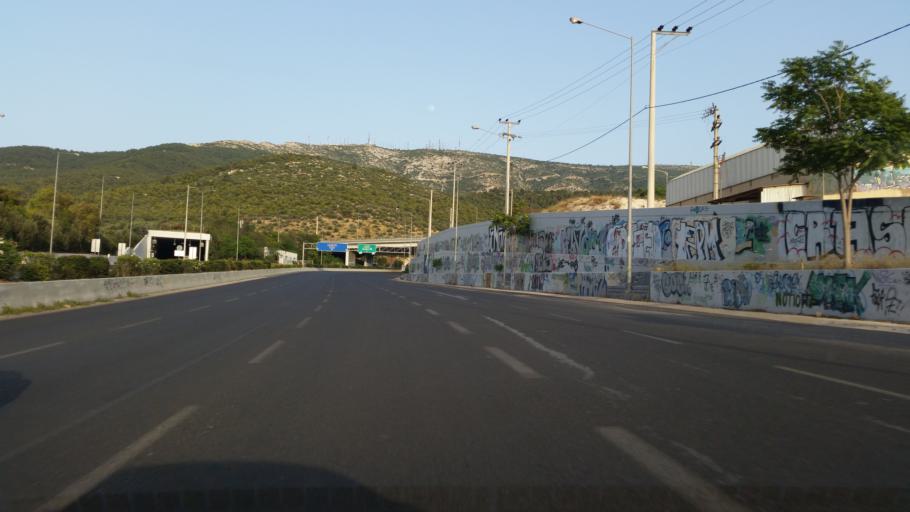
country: GR
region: Attica
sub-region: Nomos Attikis
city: Zografos
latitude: 37.9751
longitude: 23.7906
